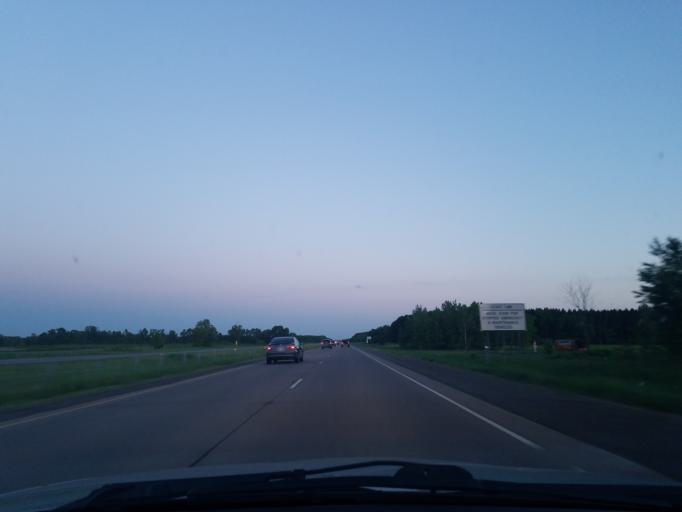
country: US
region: Minnesota
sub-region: Pine County
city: Rock Creek
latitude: 45.7297
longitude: -92.9922
